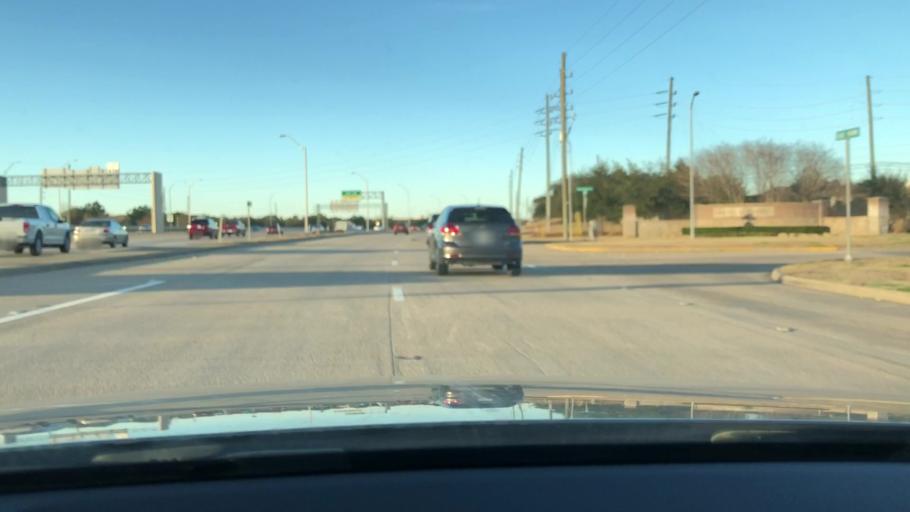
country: US
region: Texas
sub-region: Fort Bend County
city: Cinco Ranch
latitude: 29.7050
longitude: -95.7758
